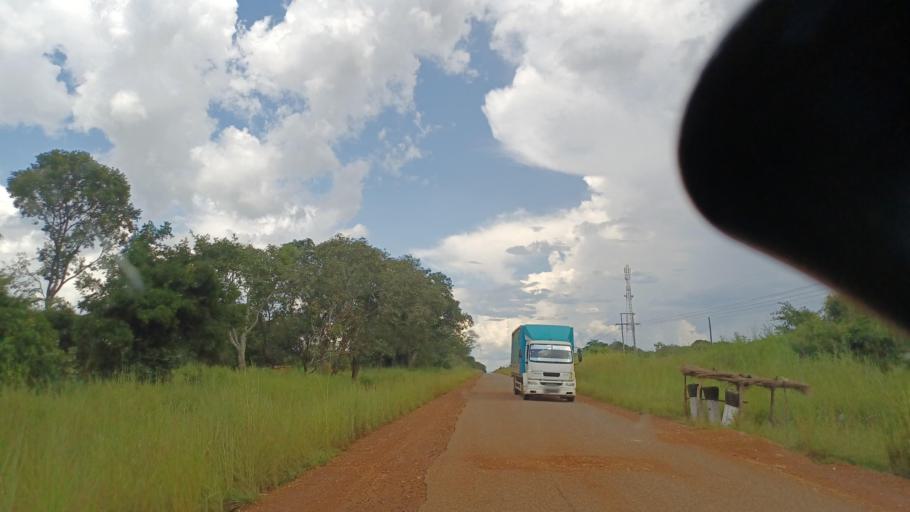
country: ZM
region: North-Western
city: Kasempa
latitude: -12.7932
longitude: 26.0151
